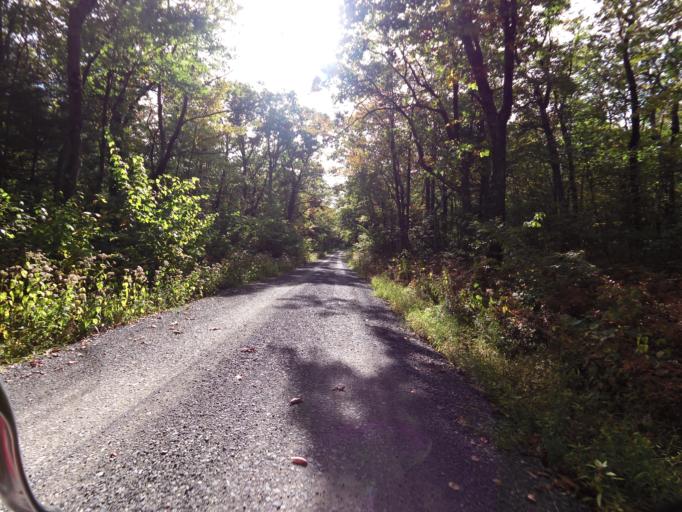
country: US
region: Pennsylvania
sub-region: Lycoming County
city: Jersey Shore
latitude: 41.1120
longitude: -77.1426
